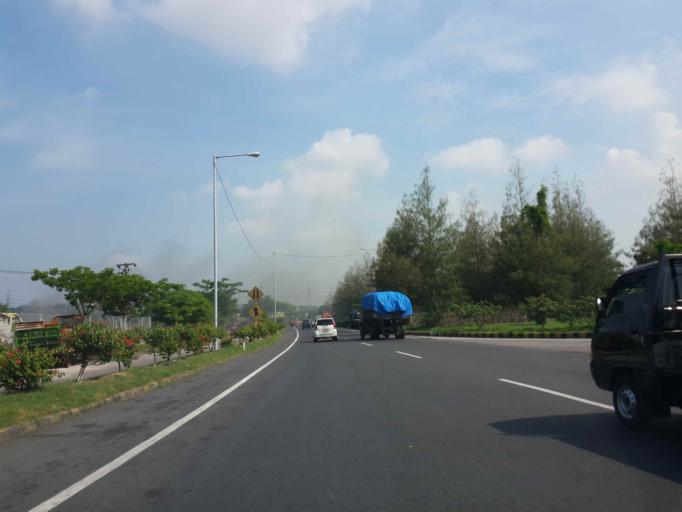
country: ID
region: East Java
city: Kebomas
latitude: -7.2014
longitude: 112.6458
